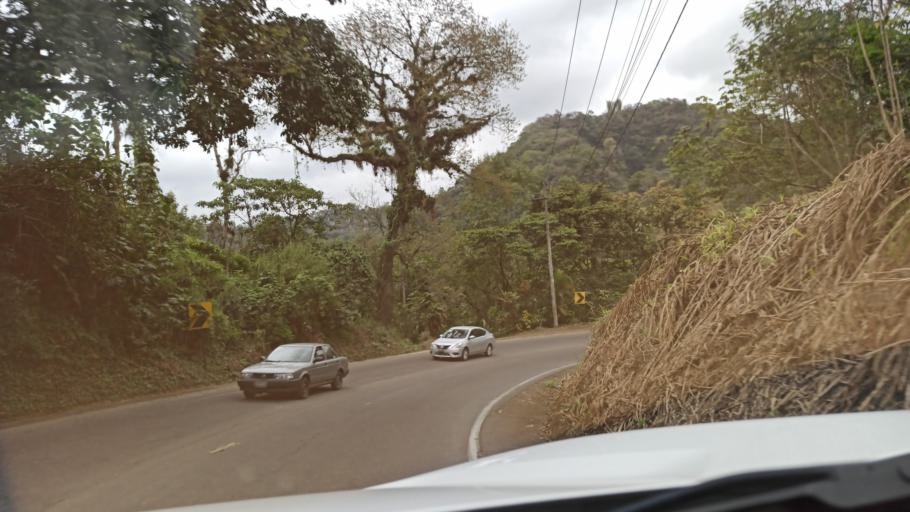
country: MX
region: Veracruz
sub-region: Fortin
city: Fortin de las Flores
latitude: 18.8957
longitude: -97.0129
